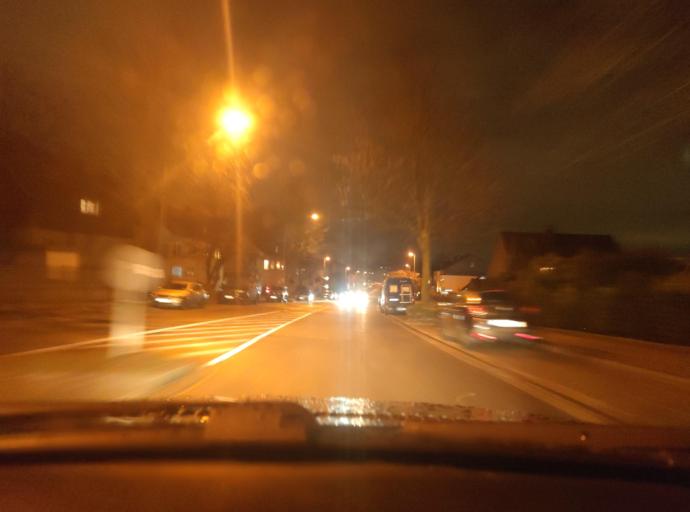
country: DE
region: North Rhine-Westphalia
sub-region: Regierungsbezirk Dusseldorf
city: Essen
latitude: 51.4758
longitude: 7.0594
